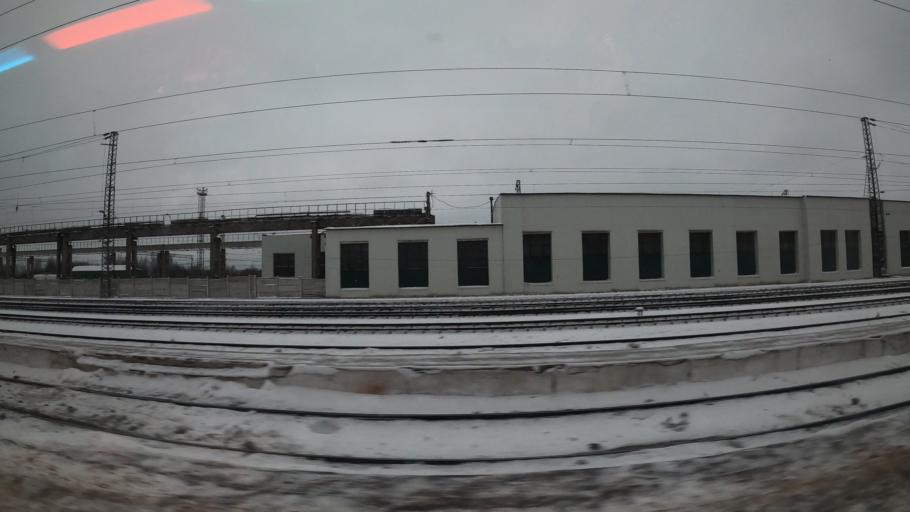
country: RU
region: Vladimir
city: Aleksandrov
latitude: 56.3983
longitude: 38.7043
